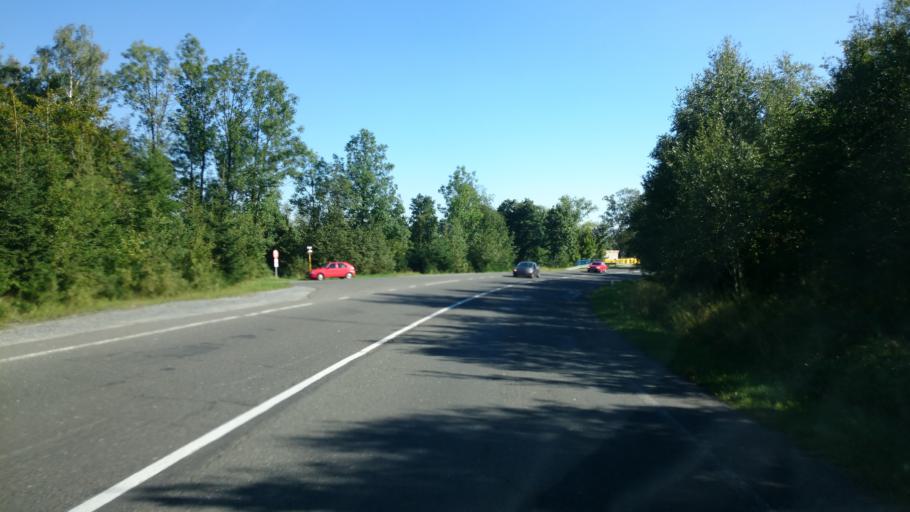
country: SK
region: Presovsky
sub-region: Okres Poprad
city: Nova Lesna
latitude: 49.1791
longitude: 20.2929
